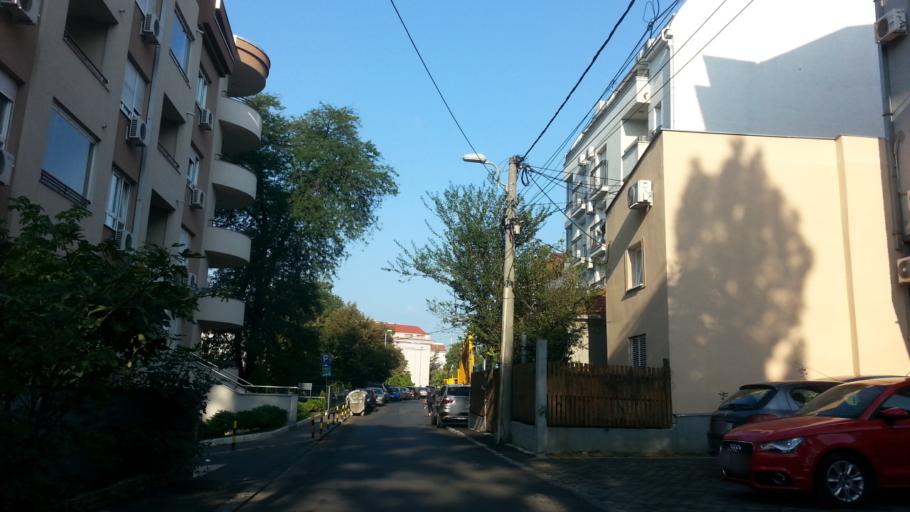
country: RS
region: Central Serbia
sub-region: Belgrade
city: Vracar
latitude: 44.7944
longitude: 20.4828
